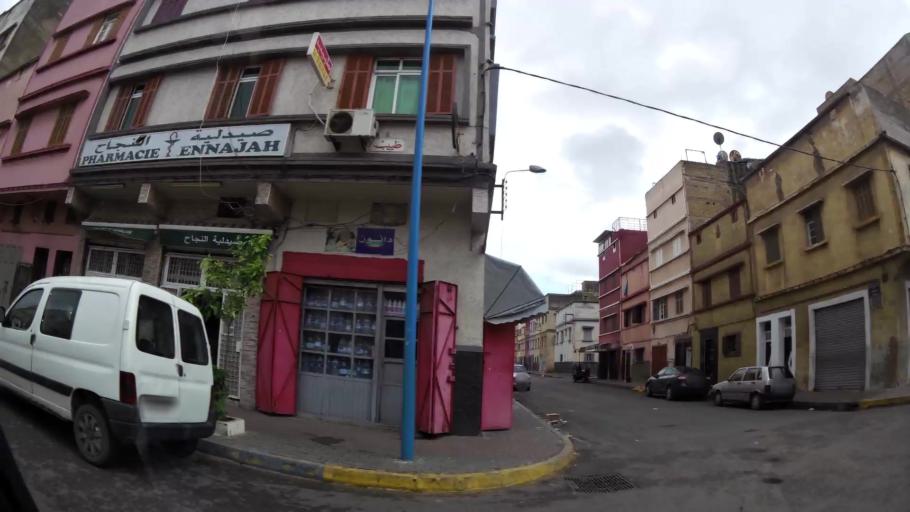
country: MA
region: Grand Casablanca
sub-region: Casablanca
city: Casablanca
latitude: 33.5484
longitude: -7.5691
